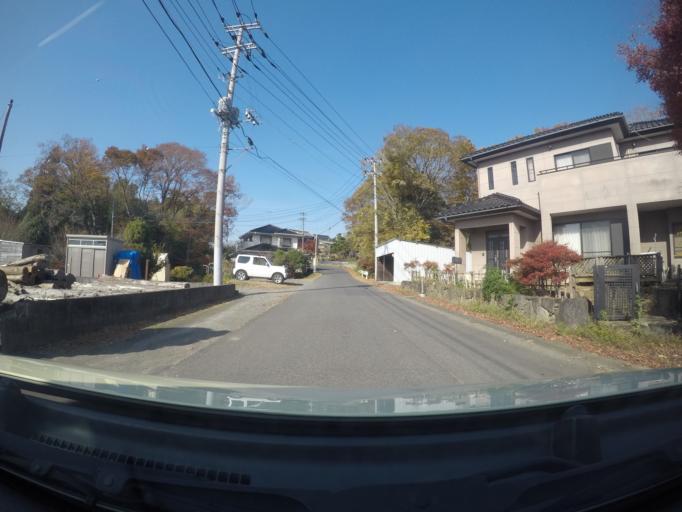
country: JP
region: Ibaraki
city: Tsukuba
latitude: 36.2042
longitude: 140.0883
